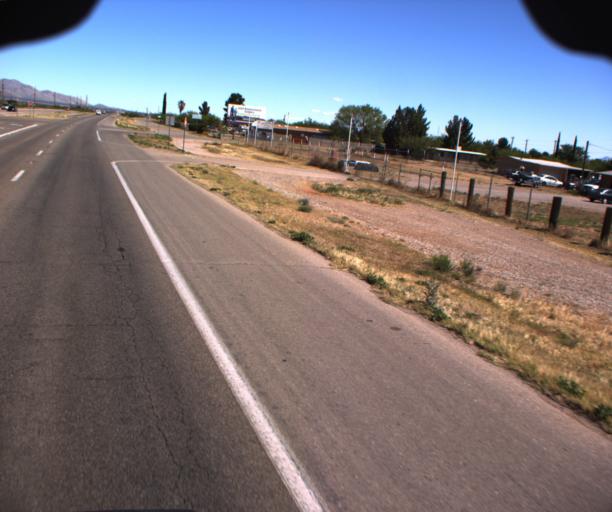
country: US
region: Arizona
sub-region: Cochise County
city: Huachuca City
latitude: 31.6860
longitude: -110.3502
